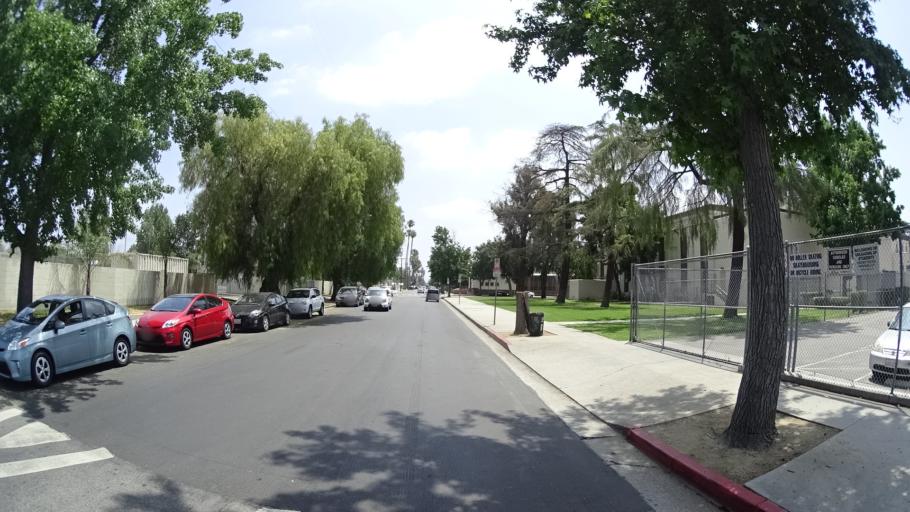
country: US
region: California
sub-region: Los Angeles County
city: Van Nuys
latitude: 34.1906
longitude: -118.4543
